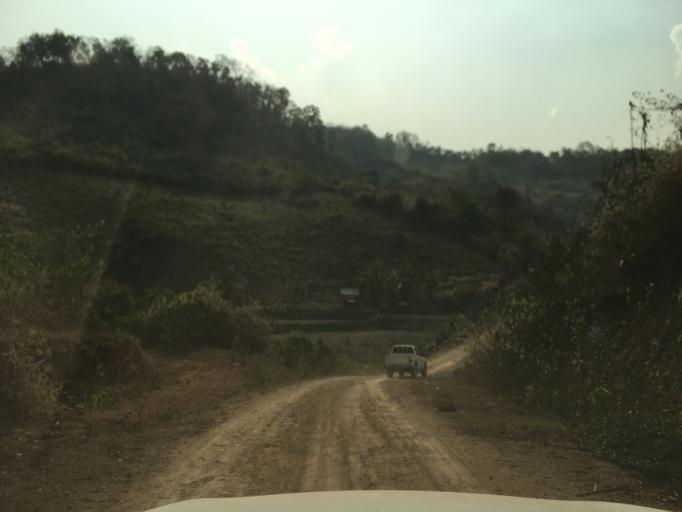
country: LA
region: Xiangkhoang
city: Phonsavan
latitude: 19.8191
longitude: 102.9974
